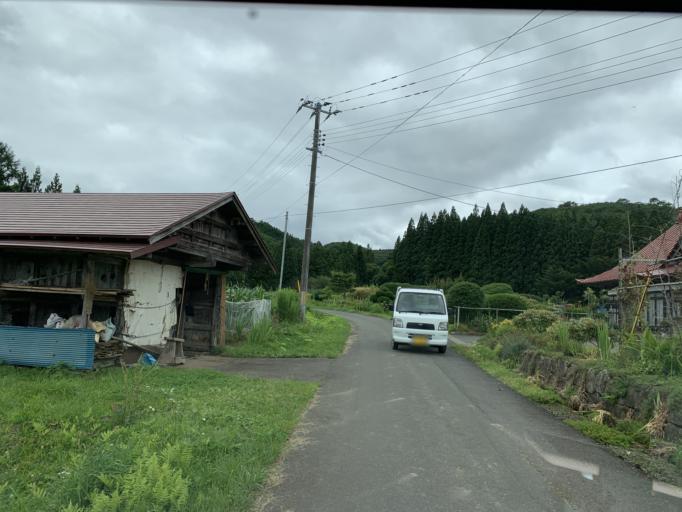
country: JP
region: Iwate
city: Ichinoseki
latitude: 38.9781
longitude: 140.9127
